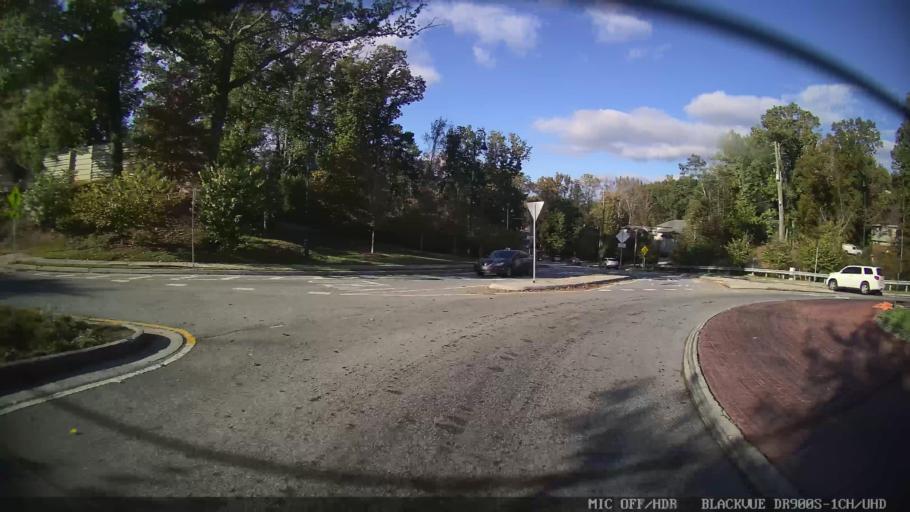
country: US
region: Georgia
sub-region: Fulton County
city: Sandy Springs
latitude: 33.9155
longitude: -84.3947
